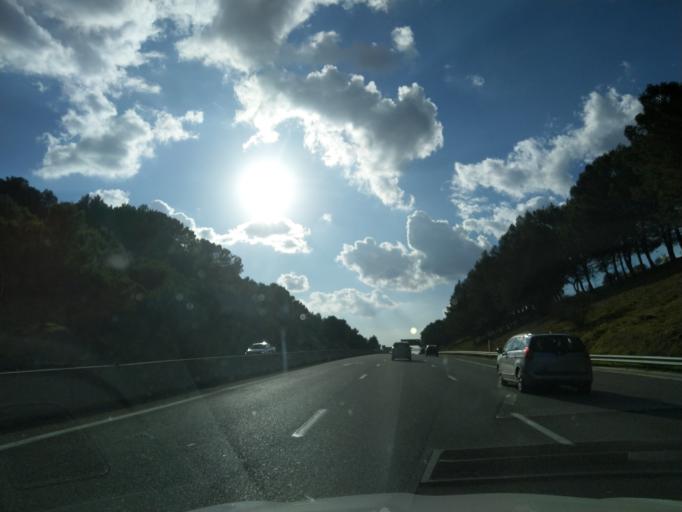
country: FR
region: Provence-Alpes-Cote d'Azur
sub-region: Departement des Bouches-du-Rhone
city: Venelles
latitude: 43.5992
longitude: 5.4928
